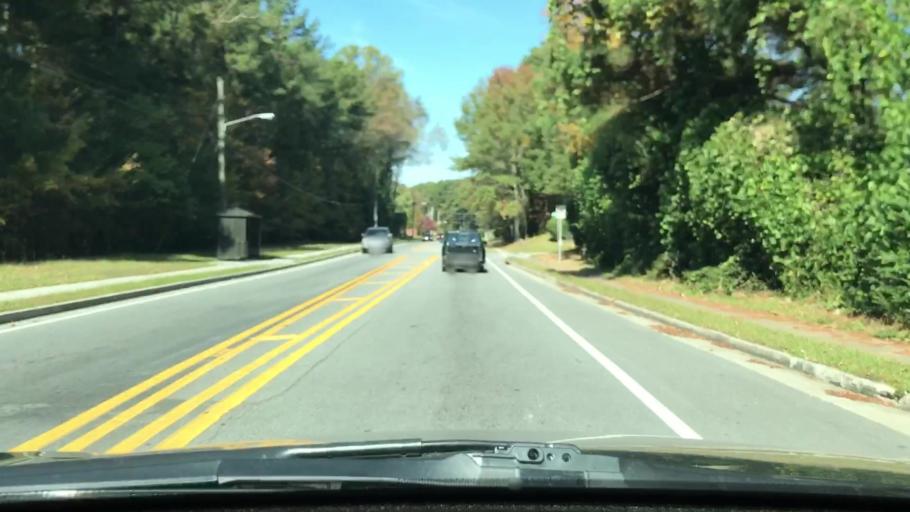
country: US
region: Georgia
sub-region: Gwinnett County
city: Norcross
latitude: 33.9260
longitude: -84.1941
